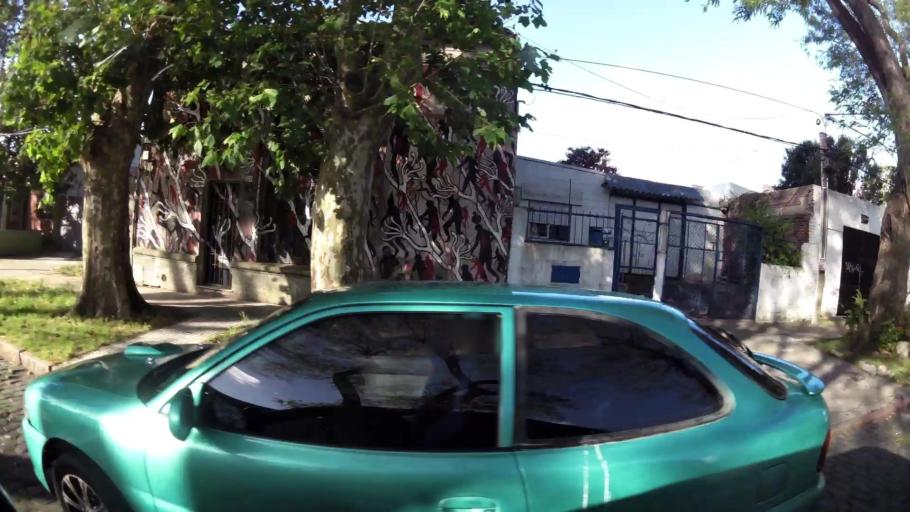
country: UY
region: Montevideo
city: Montevideo
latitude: -34.8785
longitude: -56.1577
